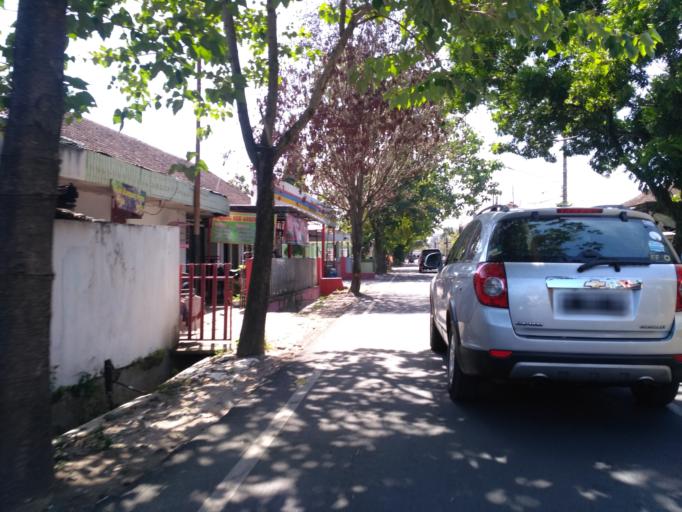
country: ID
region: East Java
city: Malang
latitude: -7.9821
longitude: 112.6478
